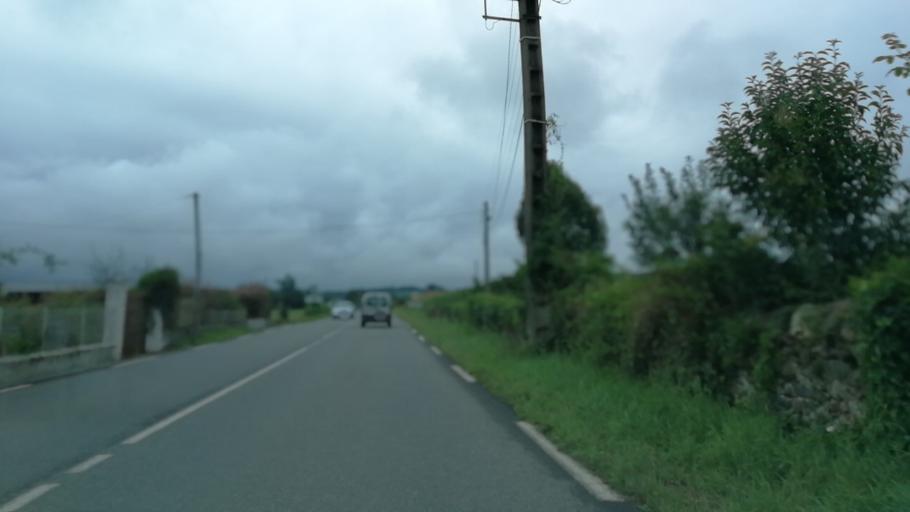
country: FR
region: Aquitaine
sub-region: Departement des Pyrenees-Atlantiques
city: Oloron-Sainte-Marie
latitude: 43.1474
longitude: -0.6003
